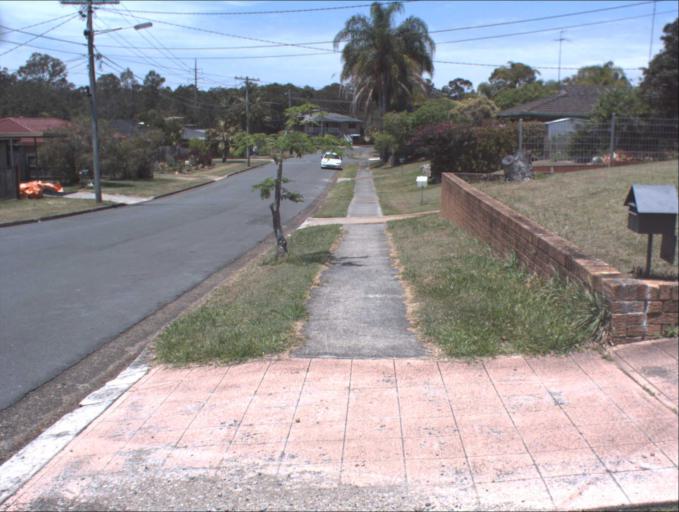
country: AU
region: Queensland
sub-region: Logan
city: Rochedale South
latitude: -27.5909
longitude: 153.1405
